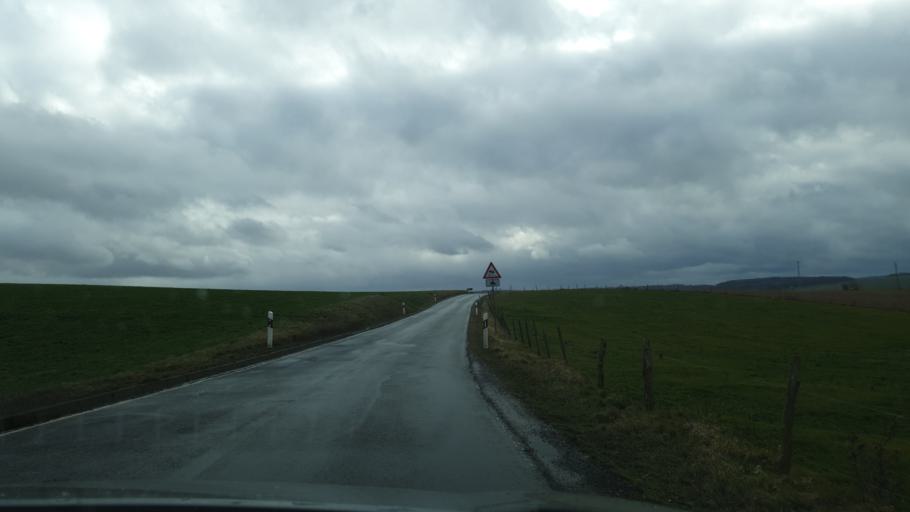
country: DE
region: Rheinland-Pfalz
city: Buch
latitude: 50.2116
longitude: 7.8702
